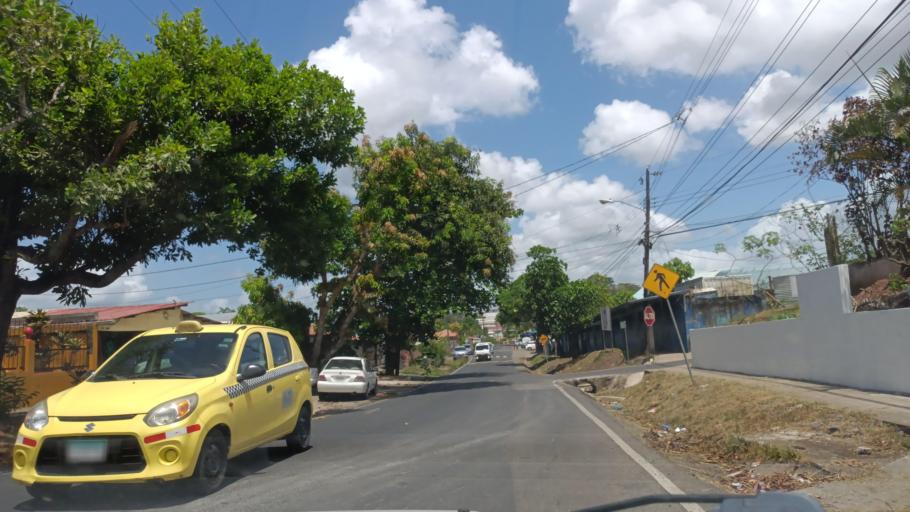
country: PA
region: Panama
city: Alcalde Diaz
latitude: 9.1047
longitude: -79.5628
